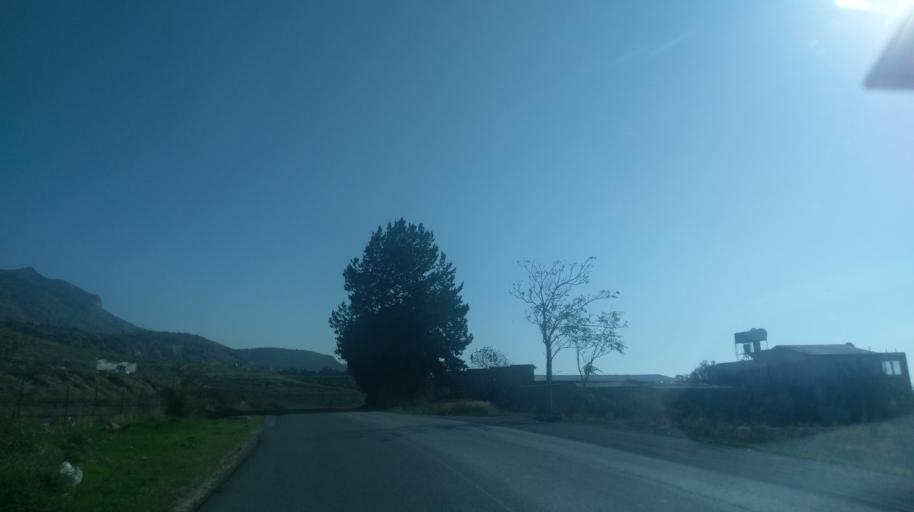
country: CY
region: Keryneia
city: Kyrenia
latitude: 35.2873
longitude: 33.2929
